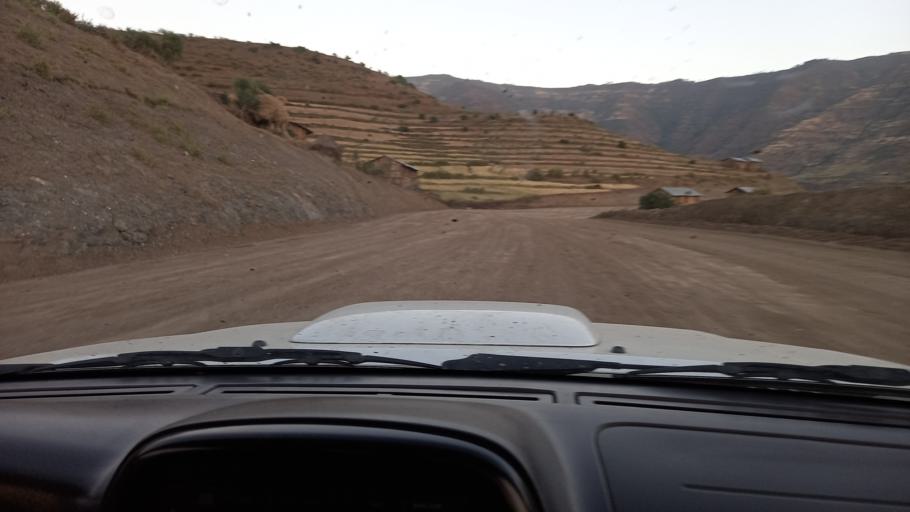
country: ET
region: Amhara
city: Debark'
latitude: 13.0379
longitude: 38.0391
